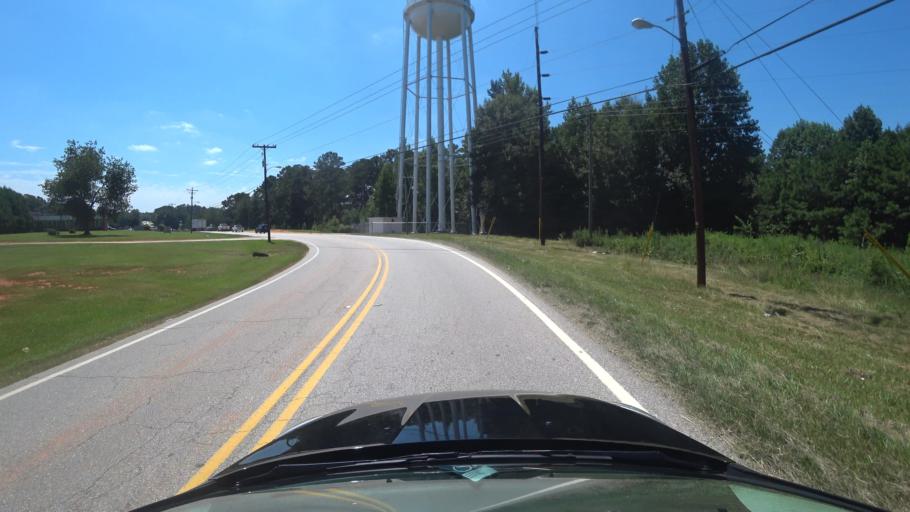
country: US
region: Georgia
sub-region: Newton County
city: Covington
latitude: 33.6123
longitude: -83.8375
